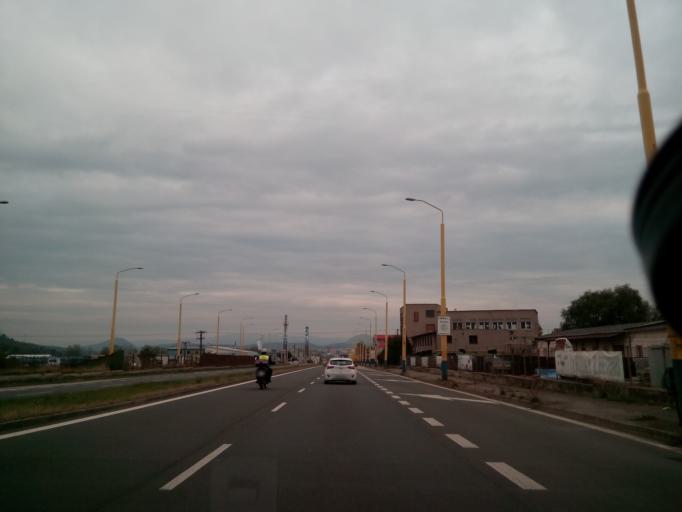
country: SK
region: Presovsky
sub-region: Okres Presov
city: Presov
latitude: 48.9617
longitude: 21.2560
